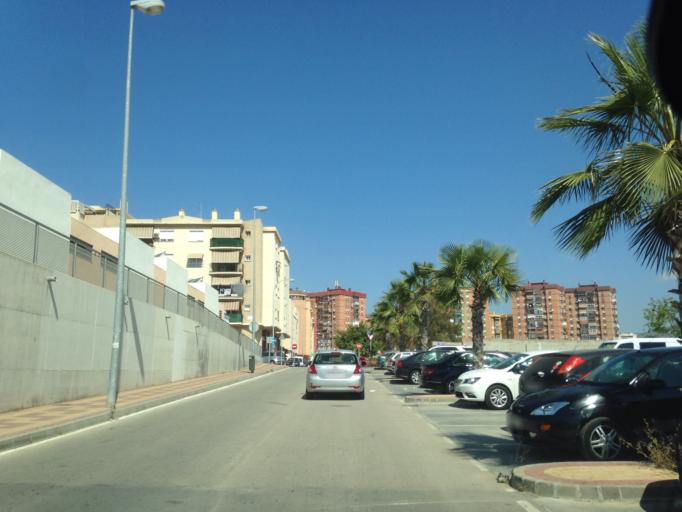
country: ES
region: Andalusia
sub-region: Provincia de Malaga
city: Malaga
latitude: 36.7016
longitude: -4.4547
